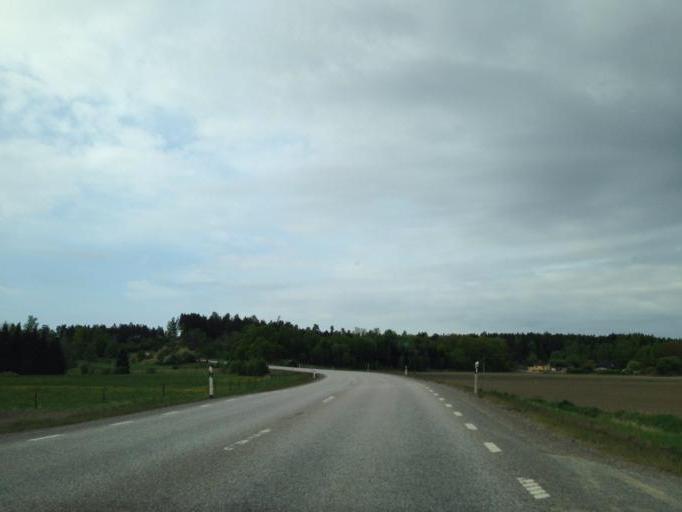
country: SE
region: Soedermanland
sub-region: Eskilstuna Kommun
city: Skogstorp
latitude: 59.3422
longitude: 16.4626
